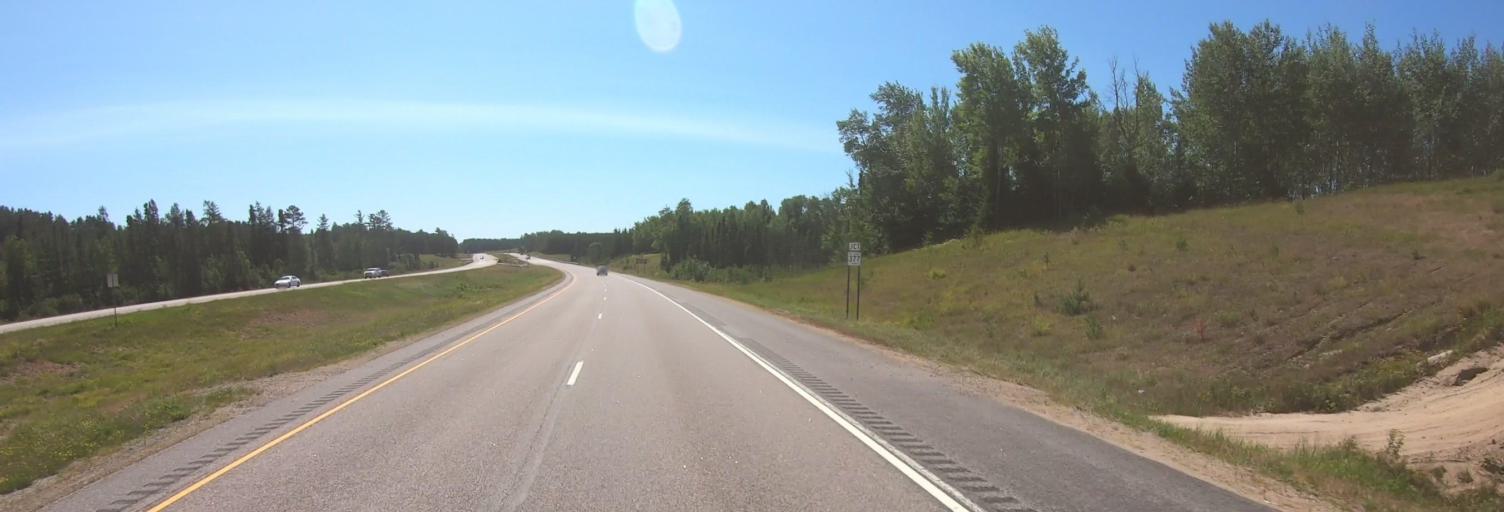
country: US
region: Minnesota
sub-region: Saint Louis County
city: Mountain Iron
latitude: 47.6767
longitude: -92.6518
